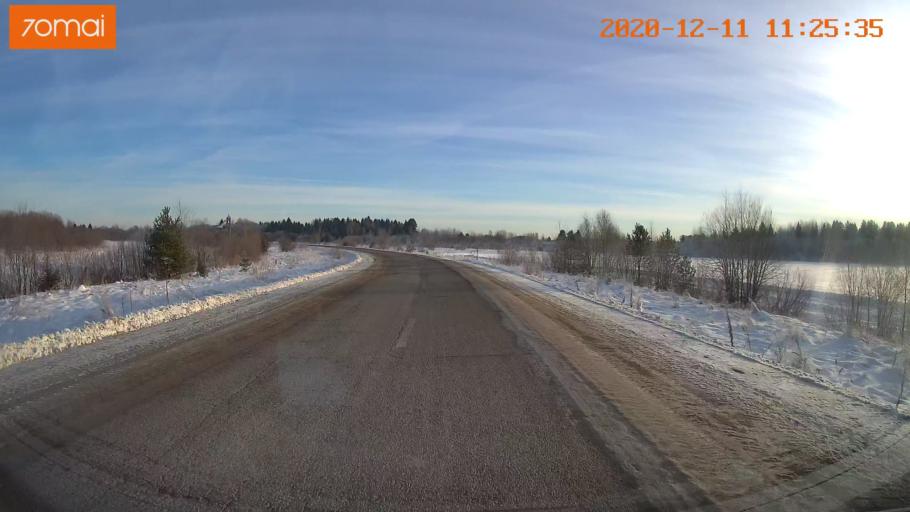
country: RU
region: Jaroslavl
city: Lyubim
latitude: 58.3386
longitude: 41.1095
